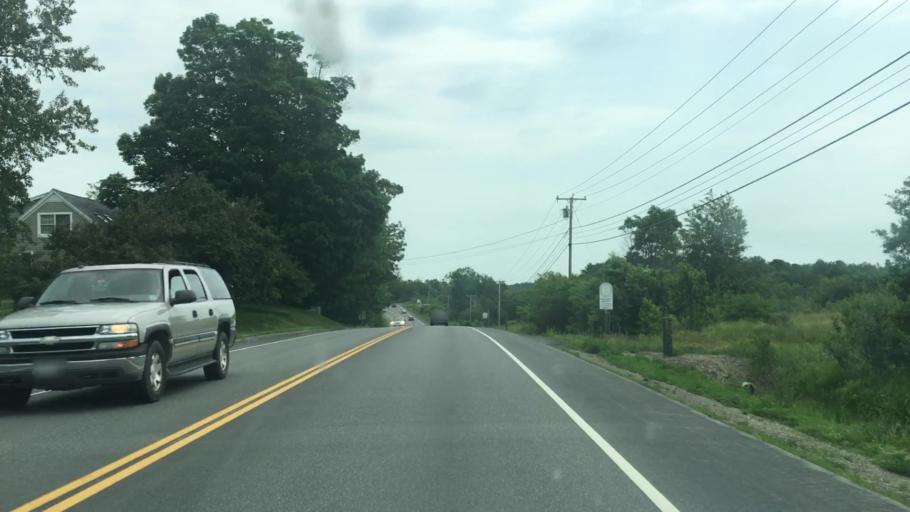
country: US
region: Maine
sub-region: Waldo County
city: Belfast
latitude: 44.4177
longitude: -69.0414
